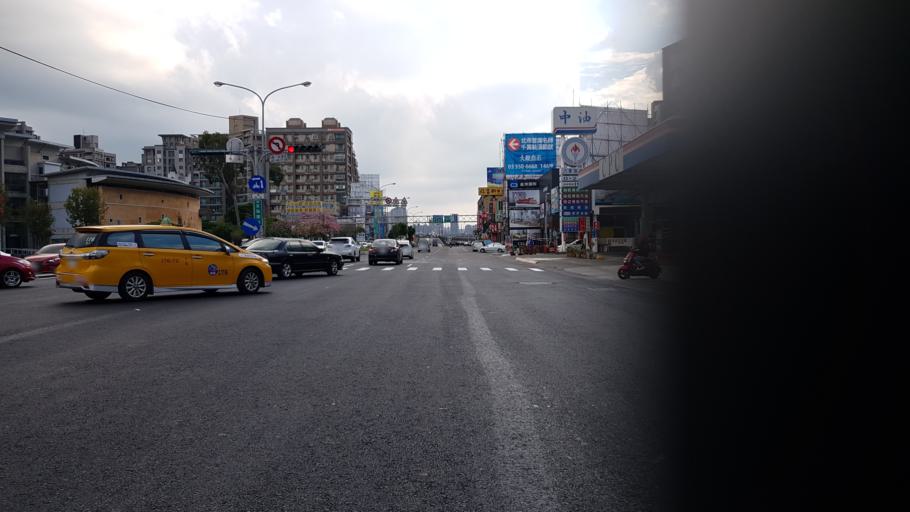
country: TW
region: Taiwan
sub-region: Hsinchu
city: Zhubei
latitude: 24.8134
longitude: 121.0233
